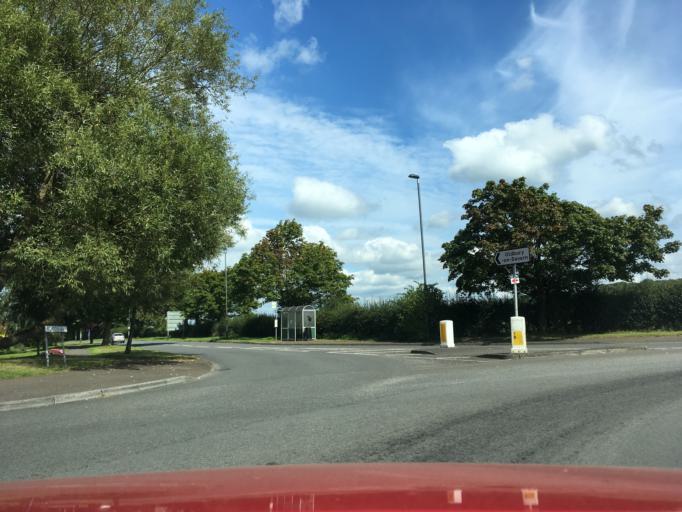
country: GB
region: England
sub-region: South Gloucestershire
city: Thornbury
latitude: 51.6032
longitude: -2.5062
